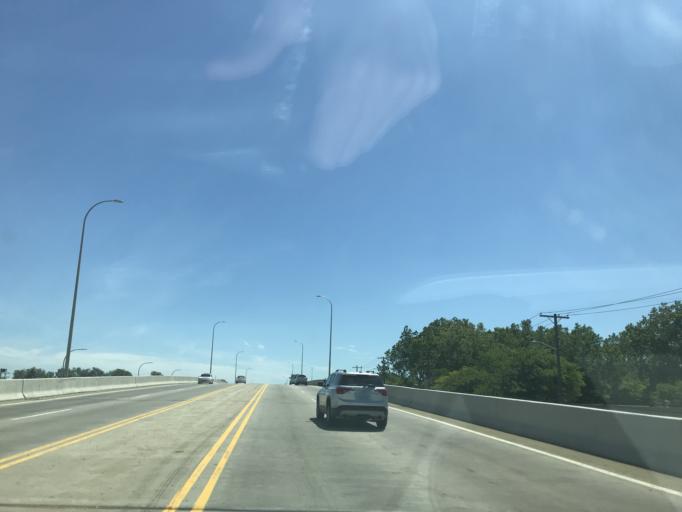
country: US
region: Michigan
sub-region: Wayne County
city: Westland
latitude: 42.3234
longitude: -83.4265
